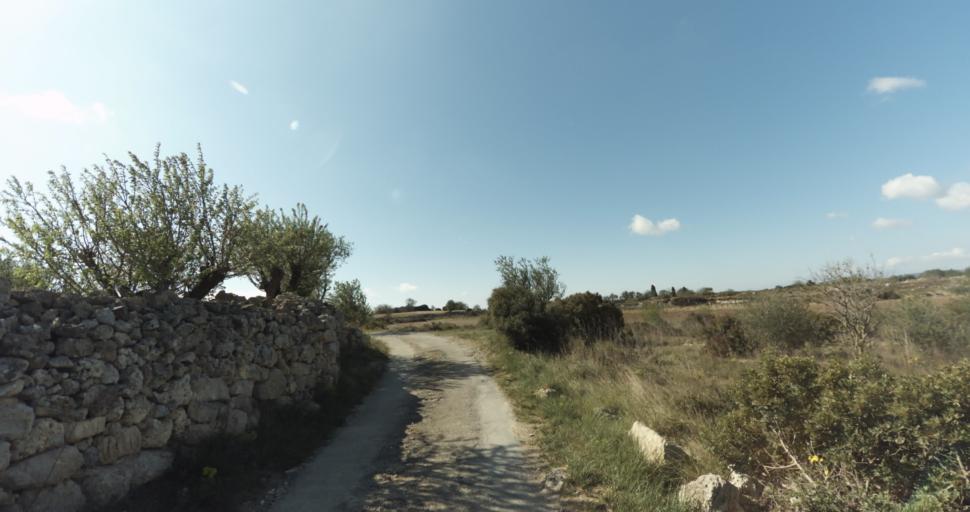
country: FR
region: Languedoc-Roussillon
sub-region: Departement de l'Aude
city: Leucate
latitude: 42.9246
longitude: 3.0317
